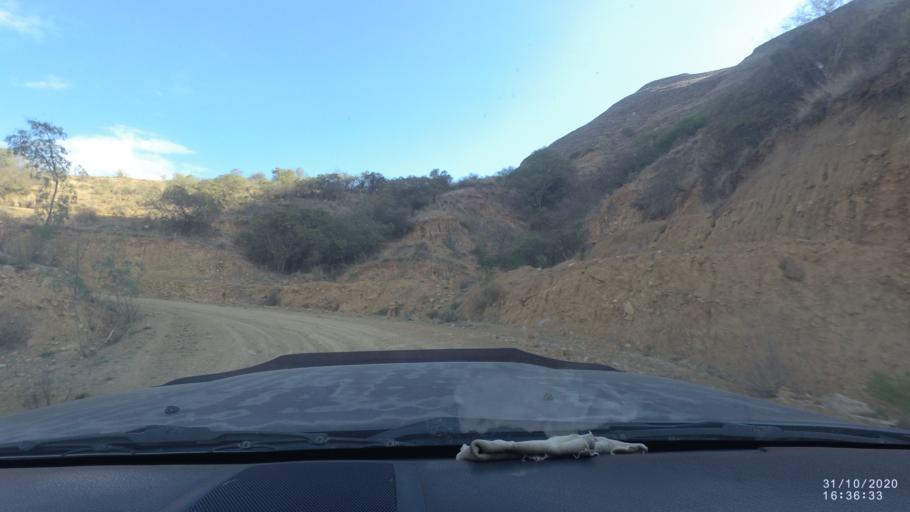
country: BO
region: Chuquisaca
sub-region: Provincia Zudanez
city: Mojocoya
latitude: -18.4602
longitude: -64.5825
